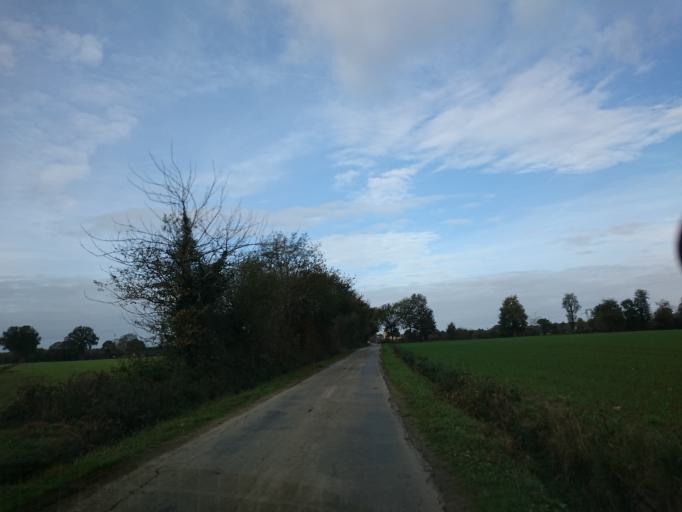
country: FR
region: Brittany
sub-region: Departement d'Ille-et-Vilaine
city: Chanteloup
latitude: 47.9390
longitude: -1.6244
